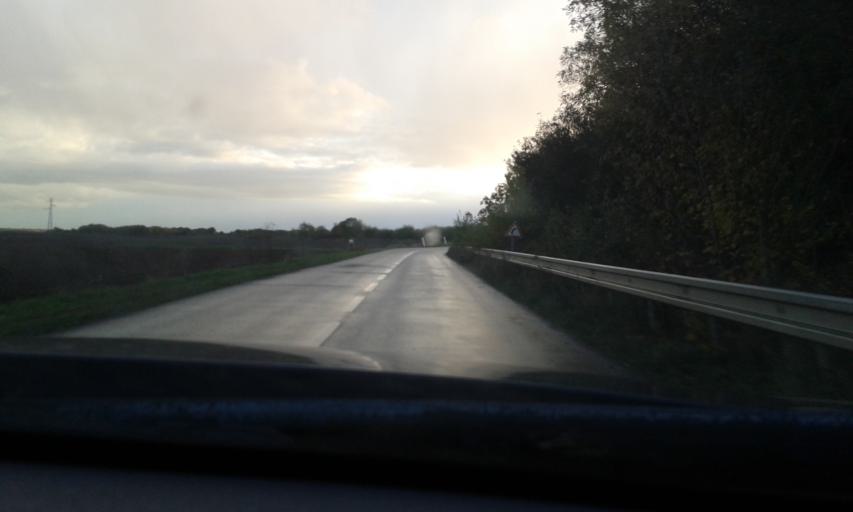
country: FR
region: Centre
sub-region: Departement du Loiret
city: Gidy
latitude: 48.0125
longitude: 1.8472
